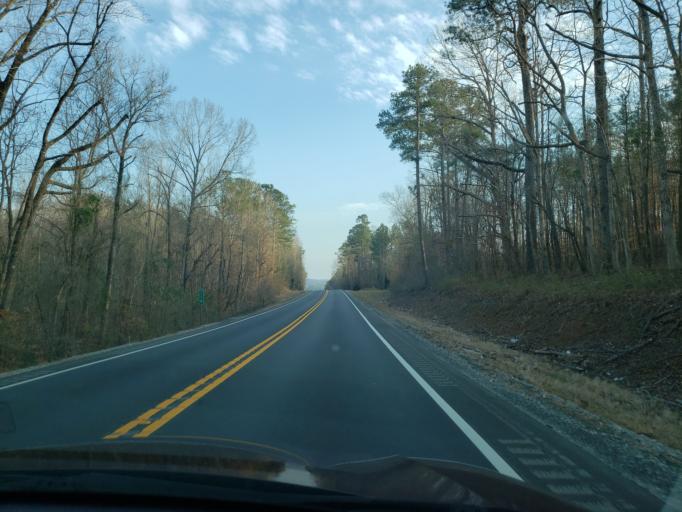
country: US
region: Alabama
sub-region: Hale County
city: Greensboro
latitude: 32.8394
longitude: -87.6082
